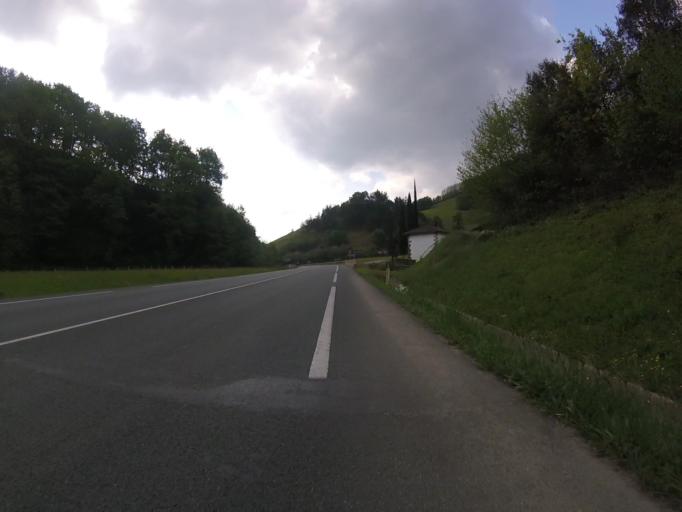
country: ES
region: Basque Country
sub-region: Provincia de Guipuzcoa
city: Azkoitia
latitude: 43.1843
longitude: -2.3240
